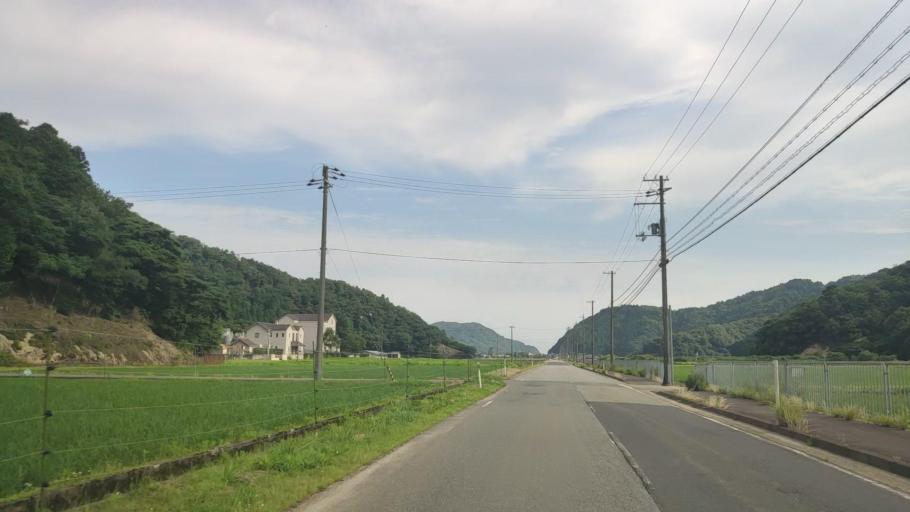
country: JP
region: Hyogo
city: Toyooka
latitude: 35.6245
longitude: 134.8412
